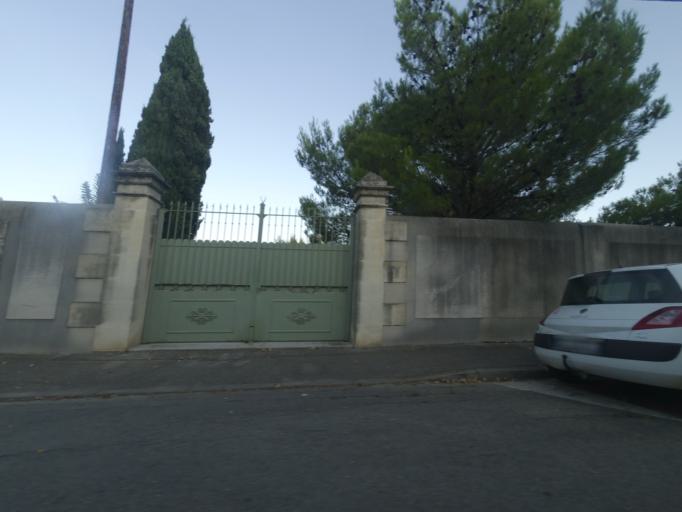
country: FR
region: Languedoc-Roussillon
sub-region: Departement du Gard
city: Calvisson
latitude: 43.7823
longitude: 4.1914
